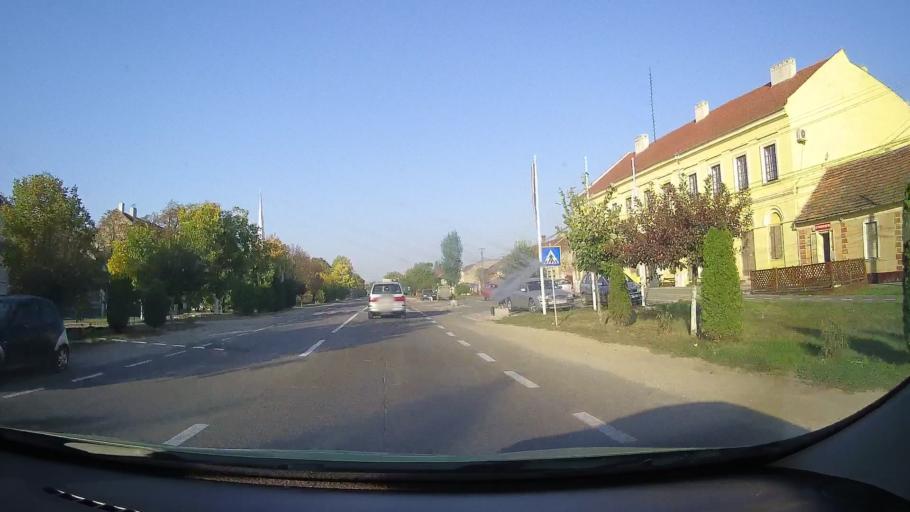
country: RO
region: Arad
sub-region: Comuna Pancota
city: Pancota
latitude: 46.3220
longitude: 21.6868
